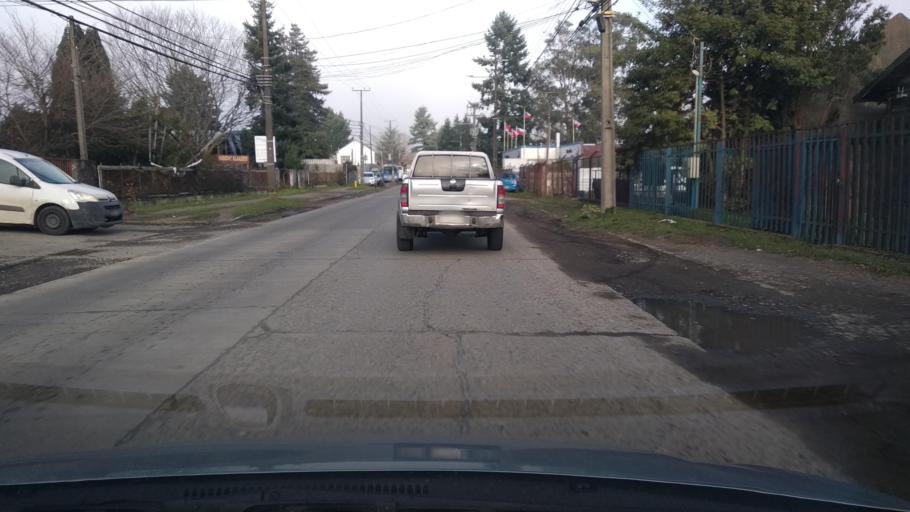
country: CL
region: Los Lagos
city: Las Animas
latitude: -39.8111
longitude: -73.2320
